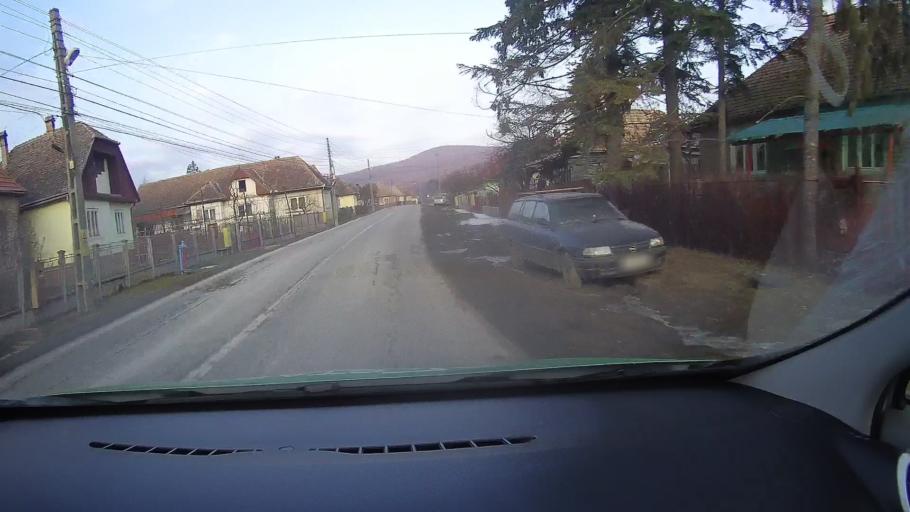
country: RO
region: Harghita
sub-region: Oras Cristuru Secuiesc
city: Cristuru Secuiesc
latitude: 46.3005
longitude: 25.0663
